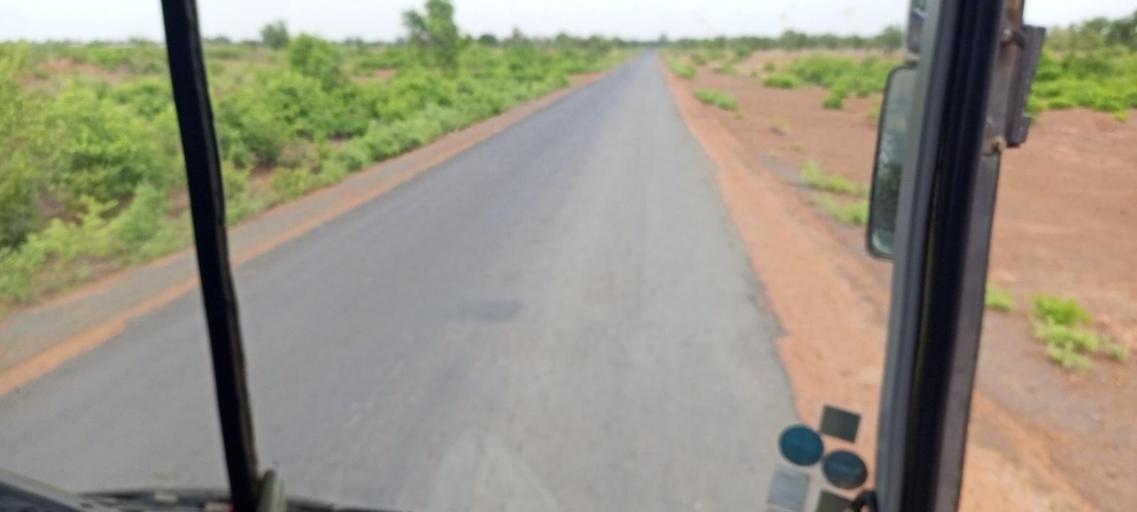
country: ML
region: Segou
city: Bla
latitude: 12.7497
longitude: -5.7328
